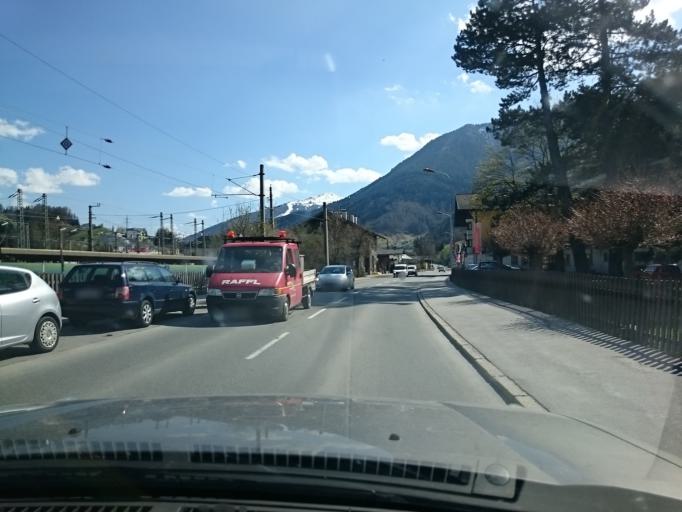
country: AT
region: Tyrol
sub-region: Politischer Bezirk Innsbruck Land
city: Matrei am Brenner
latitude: 47.1282
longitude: 11.4527
